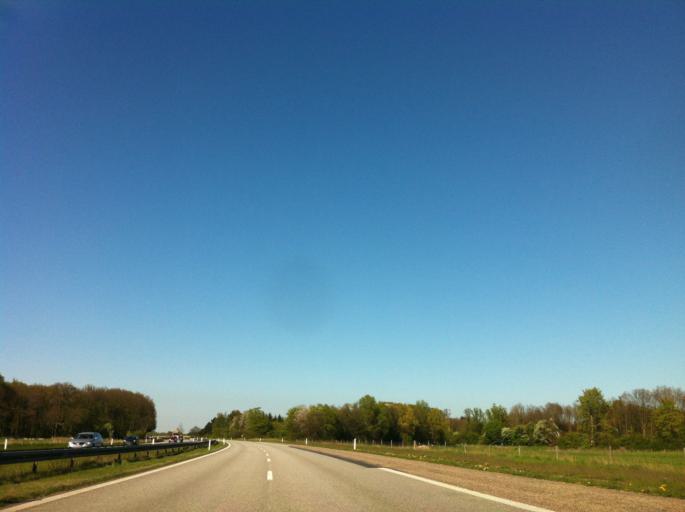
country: DK
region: Zealand
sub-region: Faxe Kommune
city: Ronnede
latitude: 55.3510
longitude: 12.0686
